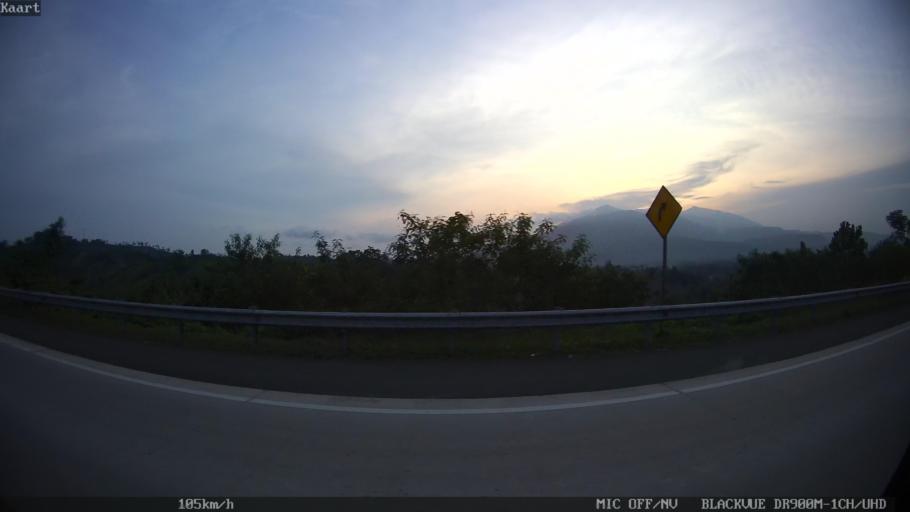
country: ID
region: Lampung
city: Penengahan
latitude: -5.7915
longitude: 105.7263
